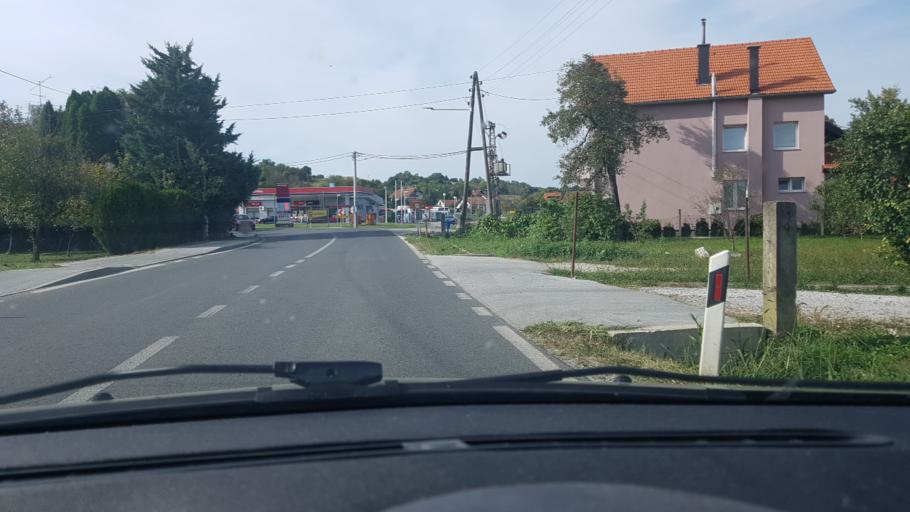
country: HR
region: Krapinsko-Zagorska
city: Zlatar
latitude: 46.1019
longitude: 16.0630
